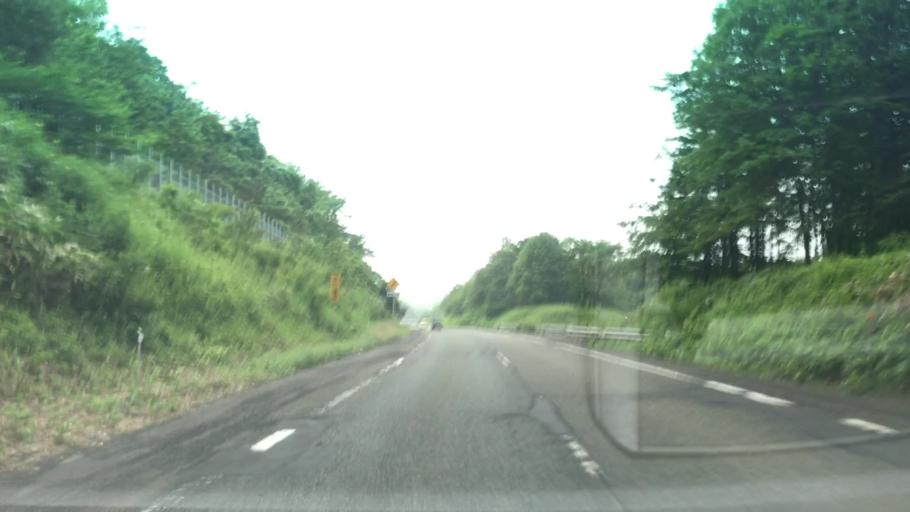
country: JP
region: Hokkaido
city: Shiraoi
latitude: 42.4753
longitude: 141.2170
